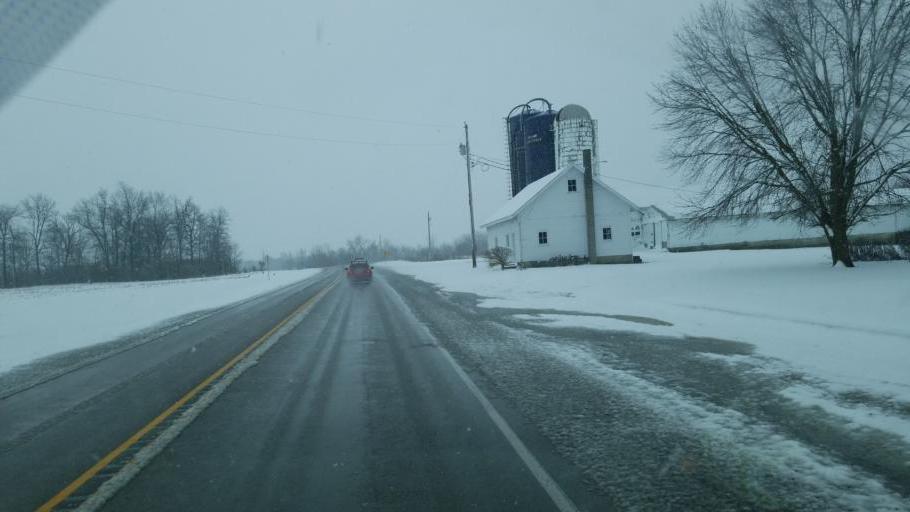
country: US
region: Indiana
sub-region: Randolph County
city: Parker City
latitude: 40.0798
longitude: -85.2747
